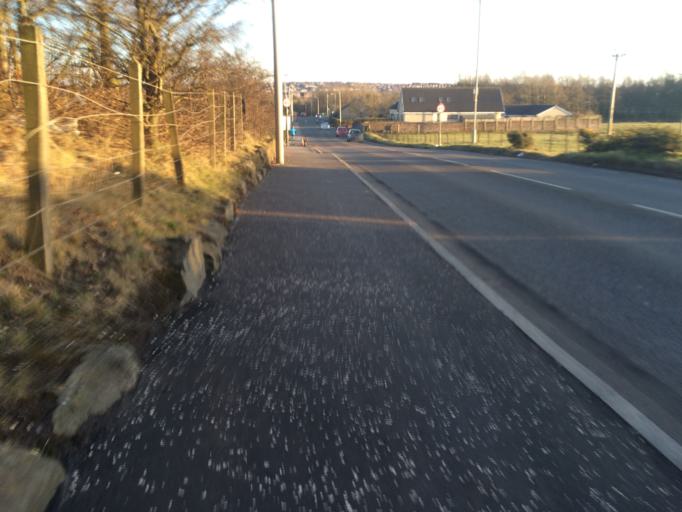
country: GB
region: Scotland
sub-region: Fife
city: Ballingry
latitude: 56.1468
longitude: -3.3245
